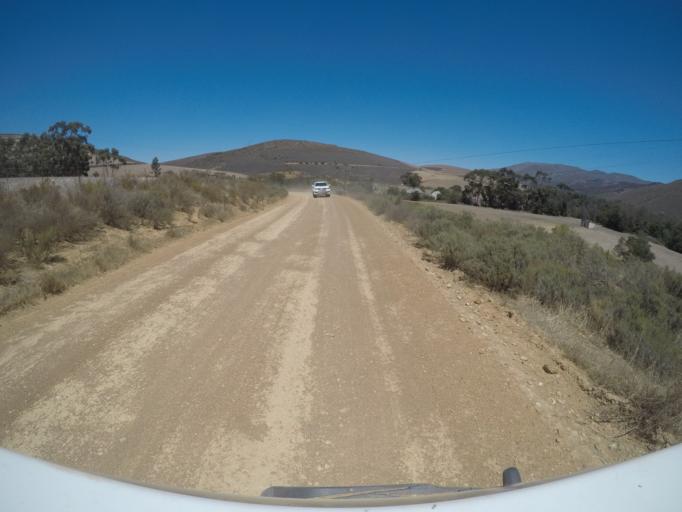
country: ZA
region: Western Cape
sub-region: Overberg District Municipality
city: Caledon
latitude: -34.1441
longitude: 19.2471
